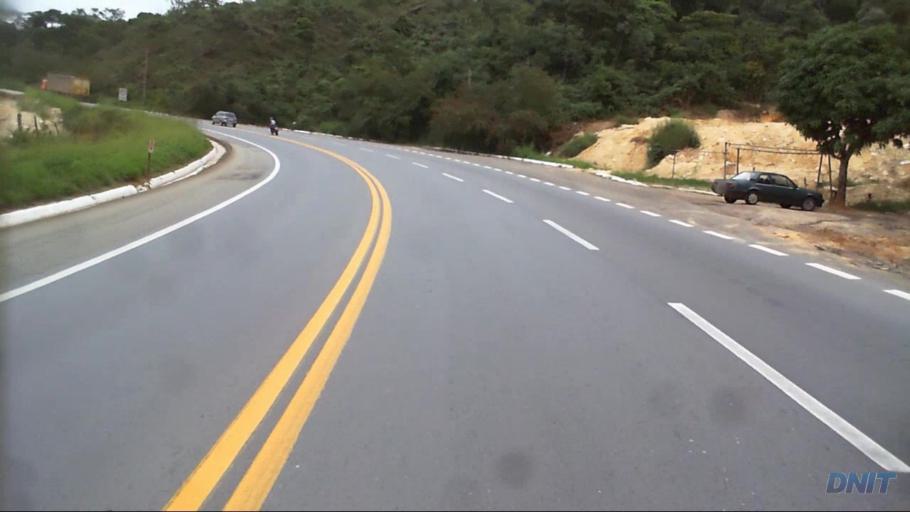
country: BR
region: Minas Gerais
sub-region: Caete
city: Caete
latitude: -19.7426
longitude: -43.5206
